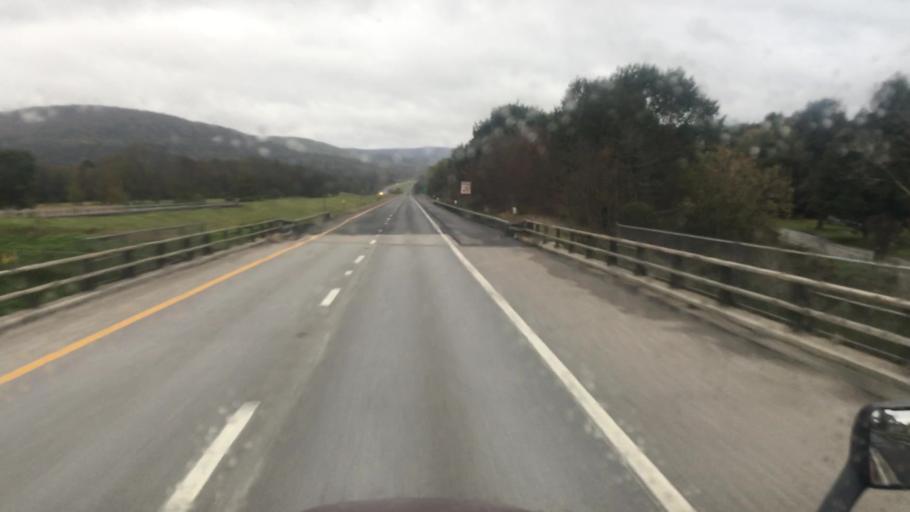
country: US
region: New York
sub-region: Otsego County
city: Unadilla
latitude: 42.3531
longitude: -75.2608
